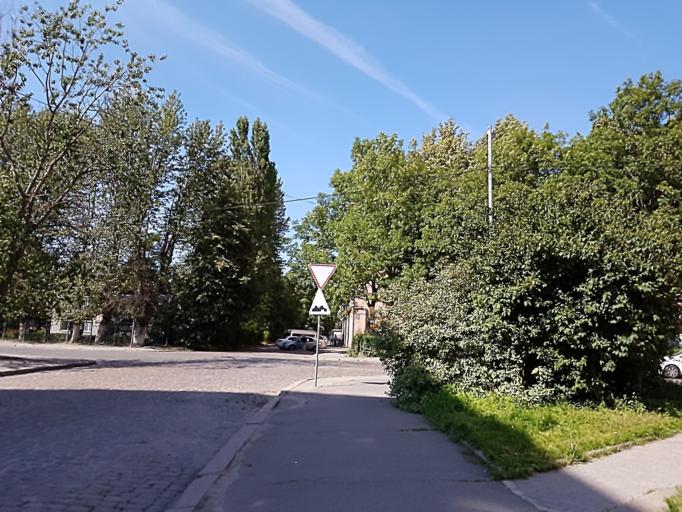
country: RU
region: Kaliningrad
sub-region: Gorod Kaliningrad
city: Kaliningrad
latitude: 54.7010
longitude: 20.5116
